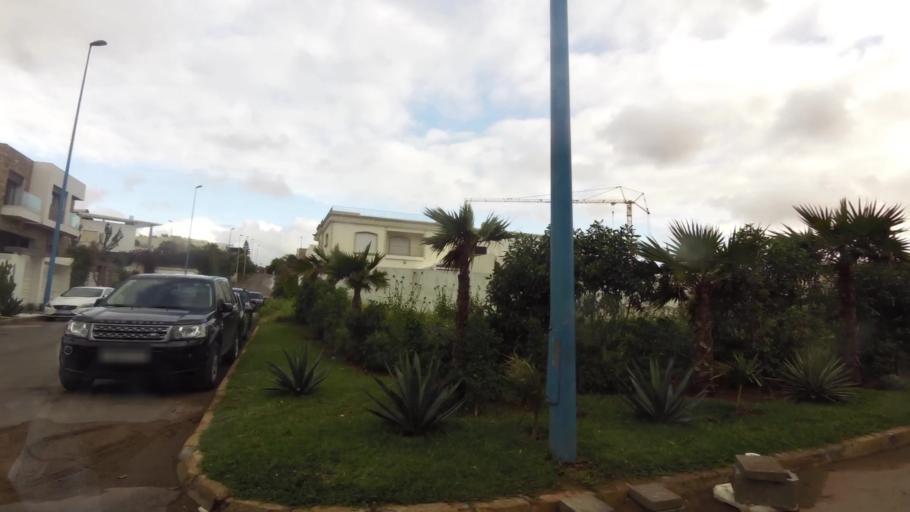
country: MA
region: Grand Casablanca
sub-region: Casablanca
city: Casablanca
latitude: 33.5860
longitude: -7.6840
